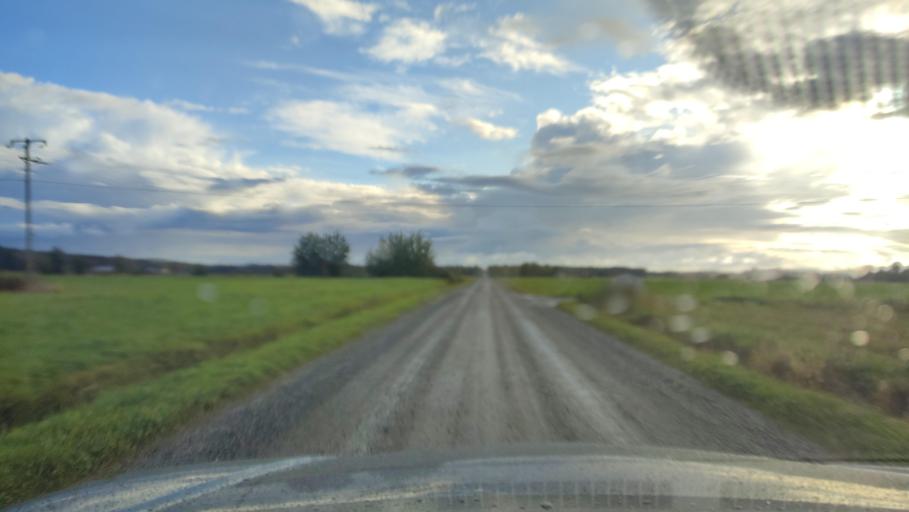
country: FI
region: Southern Ostrobothnia
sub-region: Suupohja
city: Karijoki
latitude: 62.3291
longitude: 21.5806
